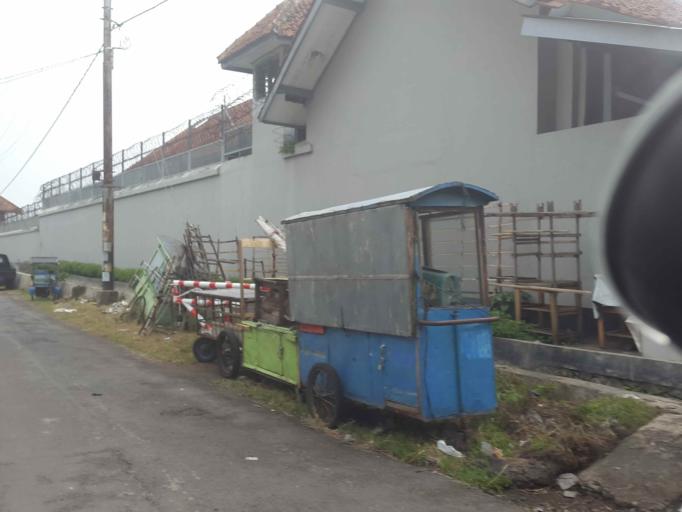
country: ID
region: Central Java
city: Purwokerto
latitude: -7.4250
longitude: 109.2294
